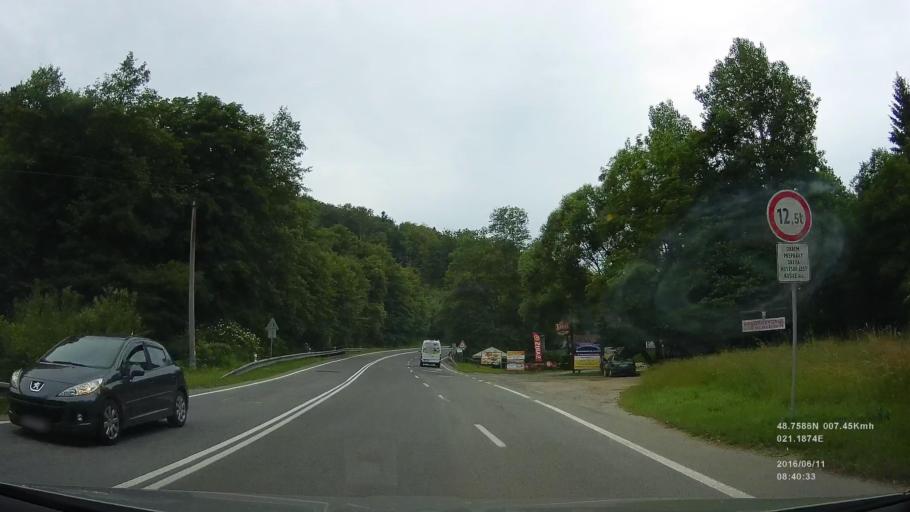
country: SK
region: Kosicky
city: Kosice
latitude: 48.7407
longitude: 21.2422
